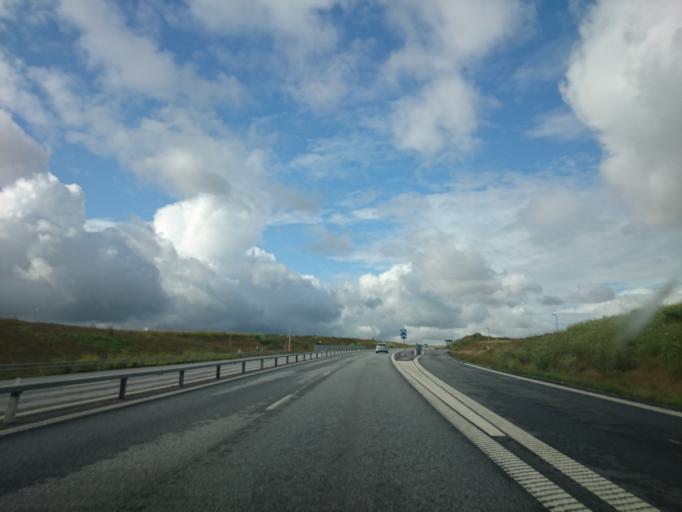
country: SE
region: Skane
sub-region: Hoors Kommun
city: Loberod
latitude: 55.7927
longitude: 13.4436
